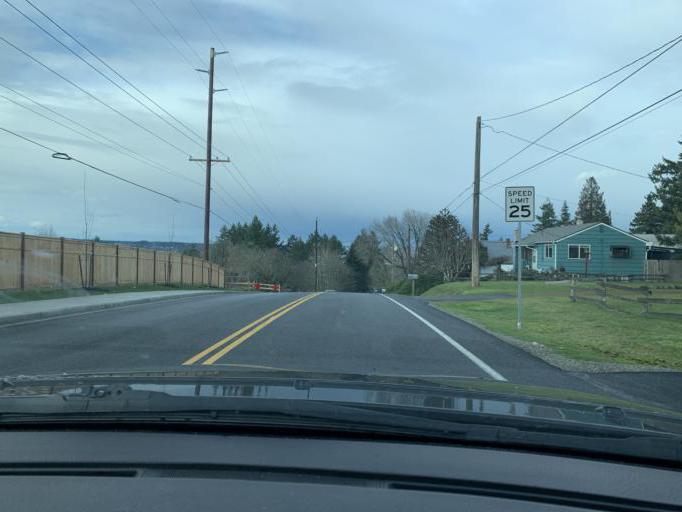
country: US
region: Washington
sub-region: Pierce County
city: Milton
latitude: 47.2391
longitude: -122.3218
